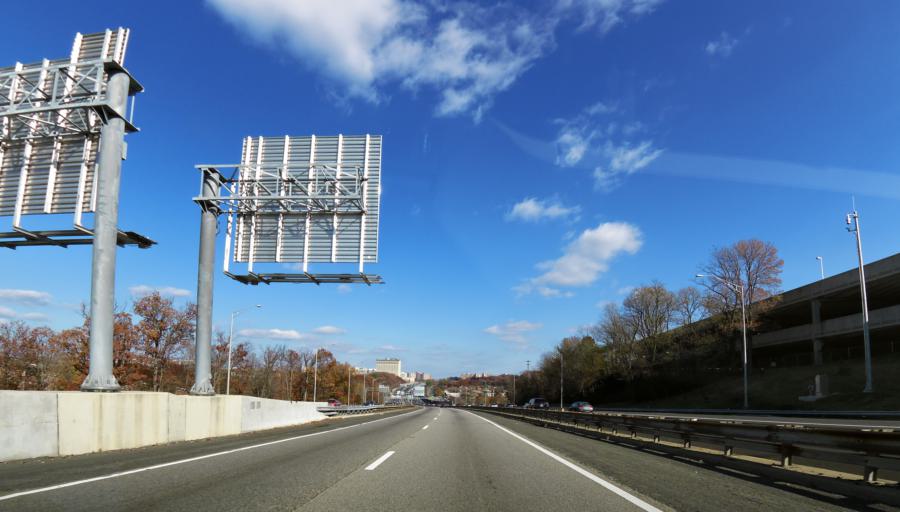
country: US
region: Virginia
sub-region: Fairfax County
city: Lincolnia
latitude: 38.8182
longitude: -77.1320
